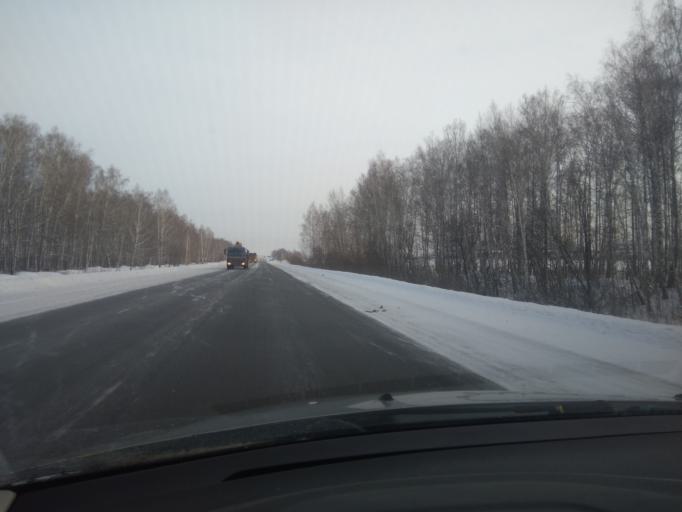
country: RU
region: Sverdlovsk
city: Bogdanovich
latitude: 56.8052
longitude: 62.0283
